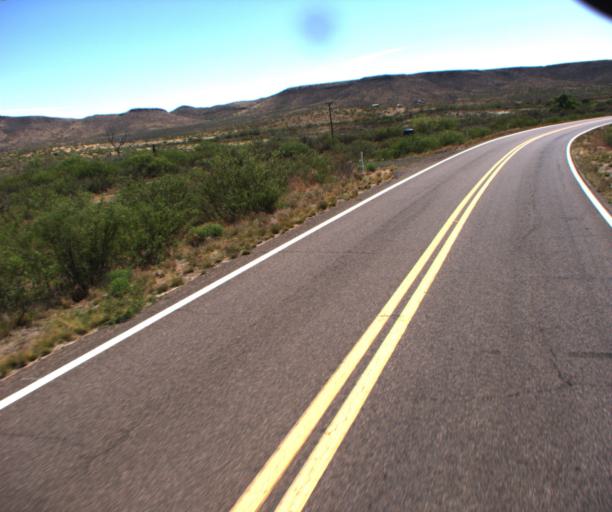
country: US
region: Arizona
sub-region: Cochise County
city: Douglas
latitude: 31.4799
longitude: -109.4055
